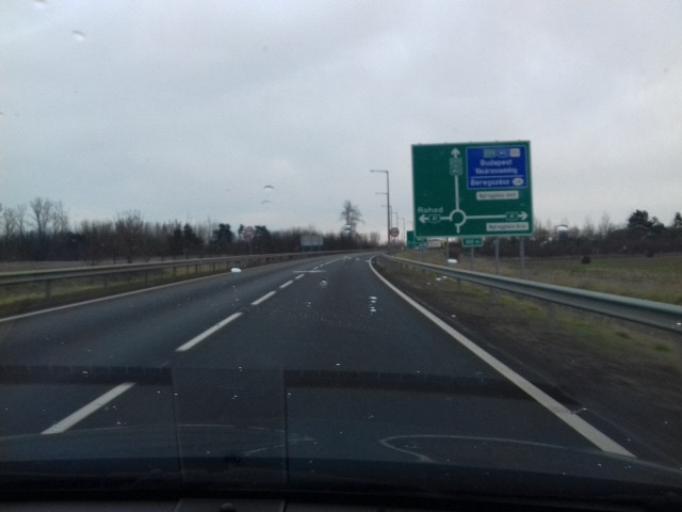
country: HU
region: Szabolcs-Szatmar-Bereg
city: Nyirpazony
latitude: 47.9539
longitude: 21.8201
